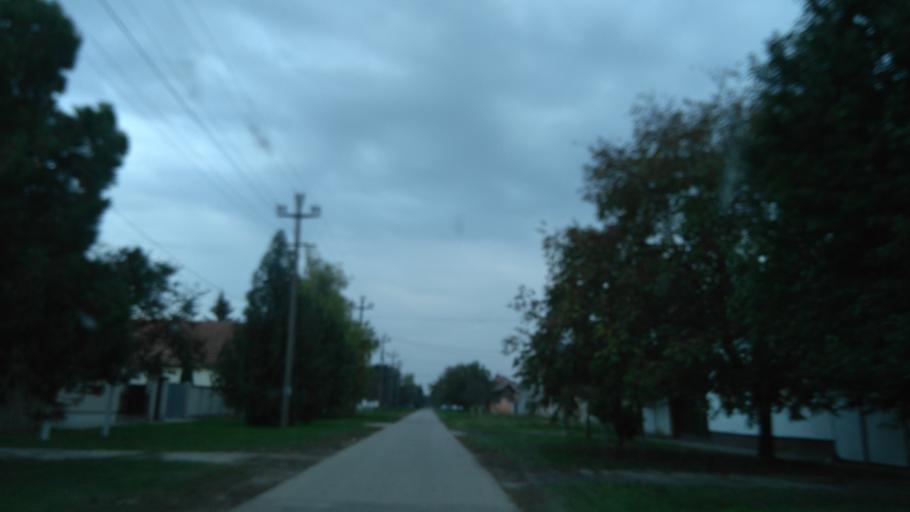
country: RS
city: Mol
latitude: 45.7602
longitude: 20.1413
